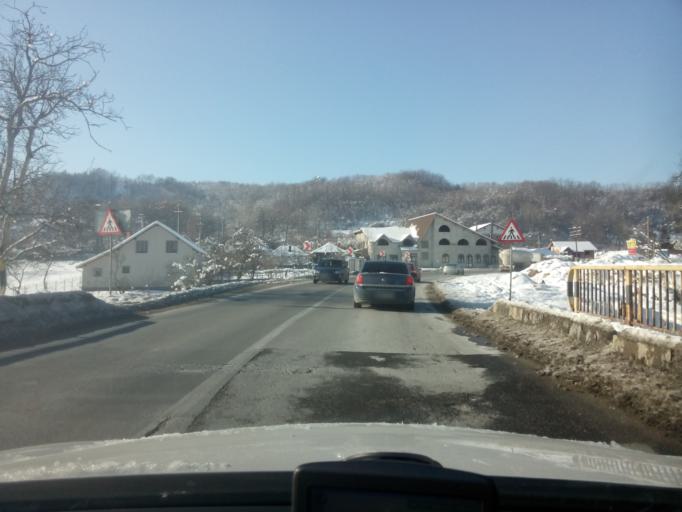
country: RO
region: Valcea
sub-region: Comuna Milcoiu
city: Milcoiu
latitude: 45.0261
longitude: 24.4849
